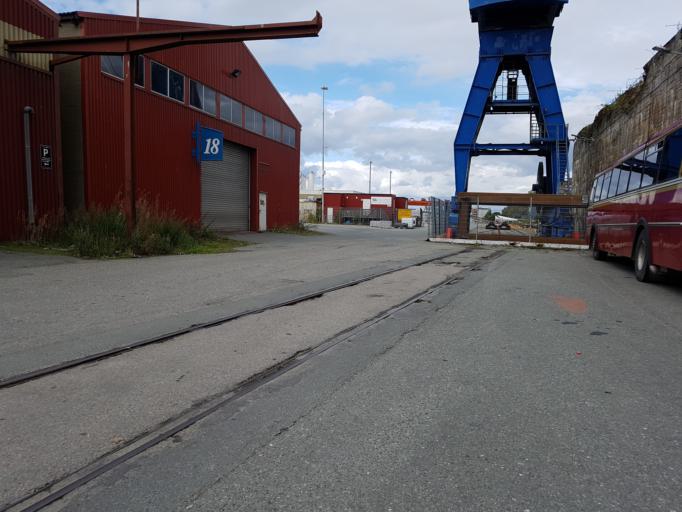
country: NO
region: Sor-Trondelag
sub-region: Trondheim
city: Trondheim
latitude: 63.4412
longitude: 10.4164
